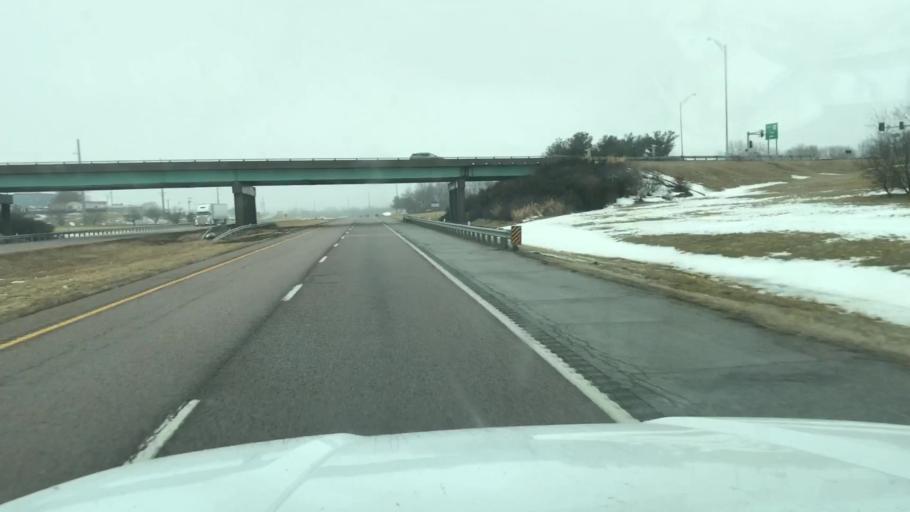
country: US
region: Missouri
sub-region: Buchanan County
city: Saint Joseph
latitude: 39.7495
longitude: -94.7670
